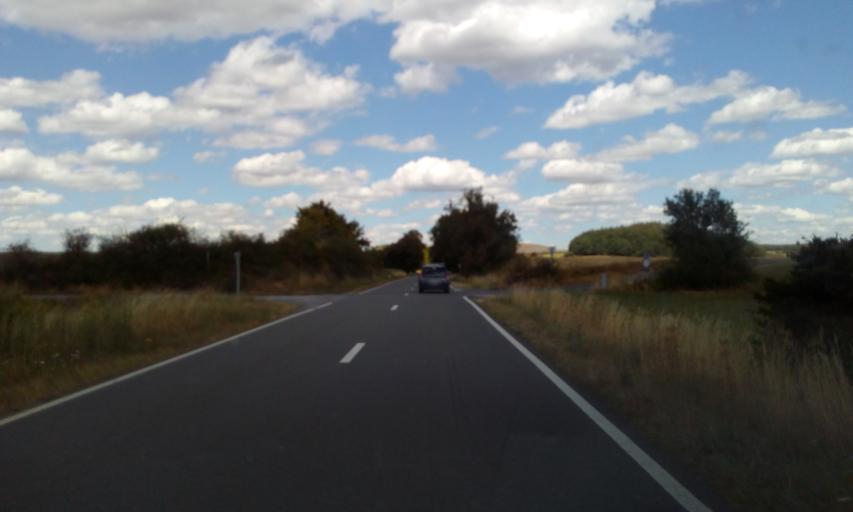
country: BE
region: Wallonia
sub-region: Province du Luxembourg
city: Wellin
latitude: 50.0857
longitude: 5.1338
